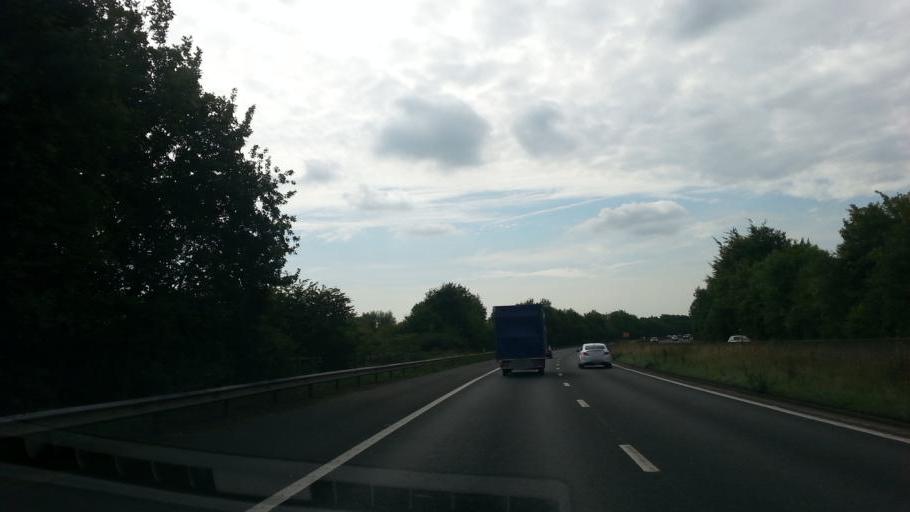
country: GB
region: England
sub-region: Hertfordshire
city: Potters Bar
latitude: 51.7107
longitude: -0.2204
